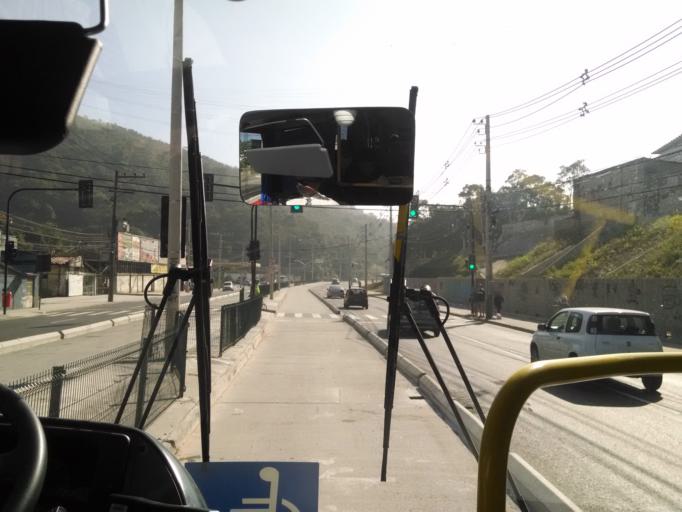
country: BR
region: Rio de Janeiro
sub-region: Sao Joao De Meriti
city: Sao Joao de Meriti
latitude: -22.9120
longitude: -43.3602
